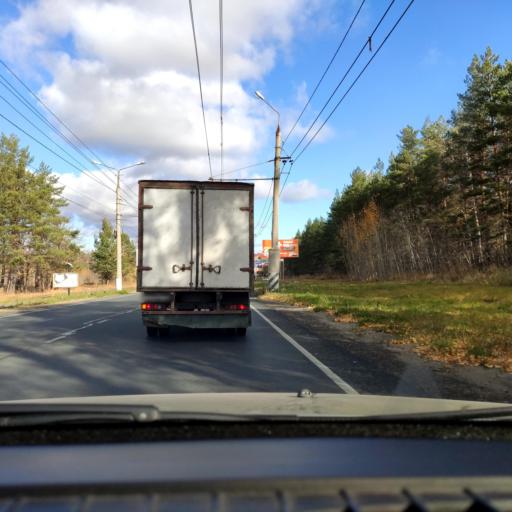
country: RU
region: Samara
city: Tol'yatti
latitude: 53.4939
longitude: 49.3865
